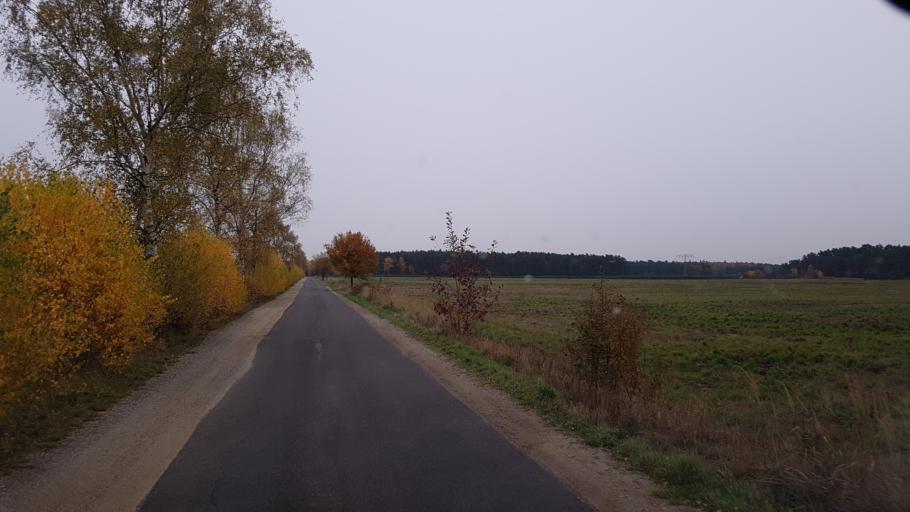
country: DE
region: Brandenburg
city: Crinitz
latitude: 51.7230
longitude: 13.7718
